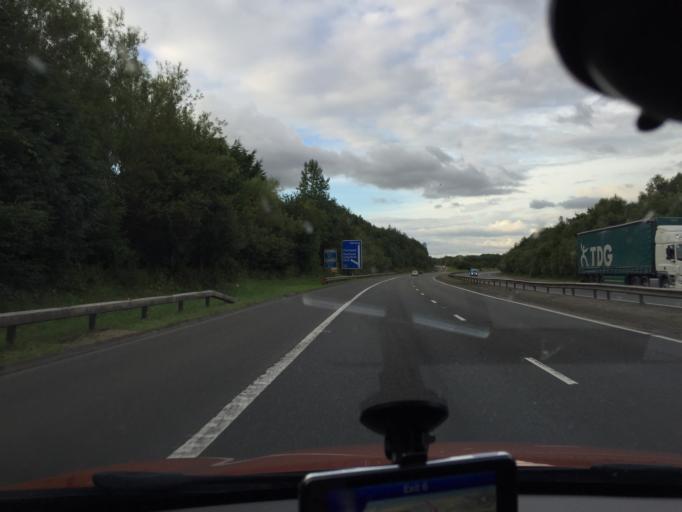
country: GB
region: Scotland
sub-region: North Lanarkshire
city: Chryston
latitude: 55.8857
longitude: -4.0808
